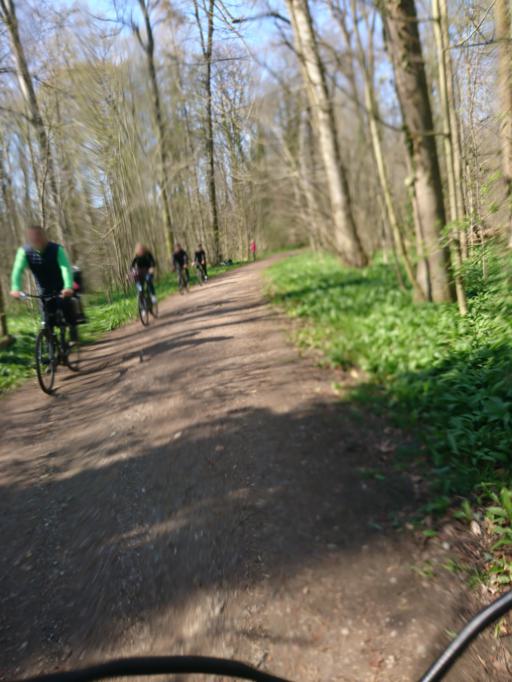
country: DE
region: Saxony
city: Markkleeberg
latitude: 51.3036
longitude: 12.3682
